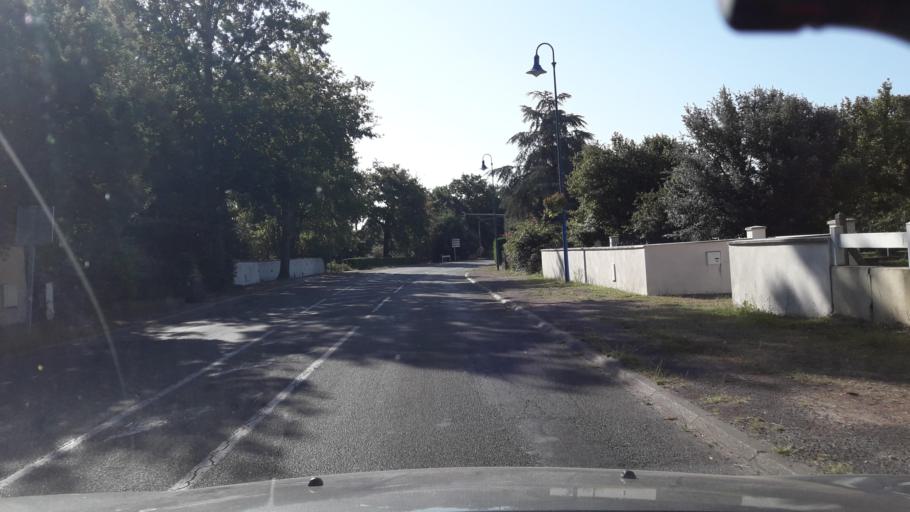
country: FR
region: Poitou-Charentes
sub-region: Departement de la Charente-Maritime
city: Etaules
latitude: 45.7281
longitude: -1.0913
